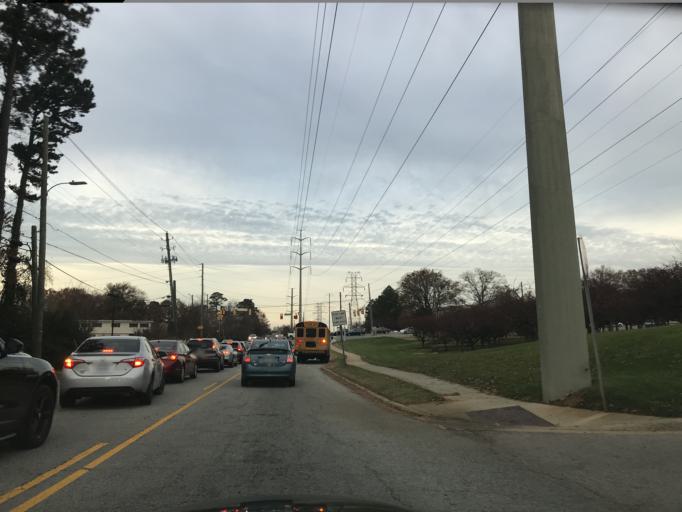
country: US
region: North Carolina
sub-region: Wake County
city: West Raleigh
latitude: 35.7839
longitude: -78.6870
